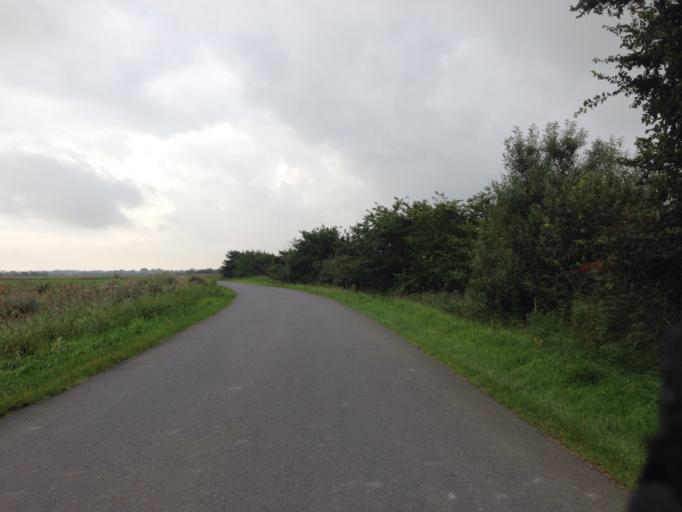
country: DE
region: Schleswig-Holstein
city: Oevenum
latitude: 54.7266
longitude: 8.5454
